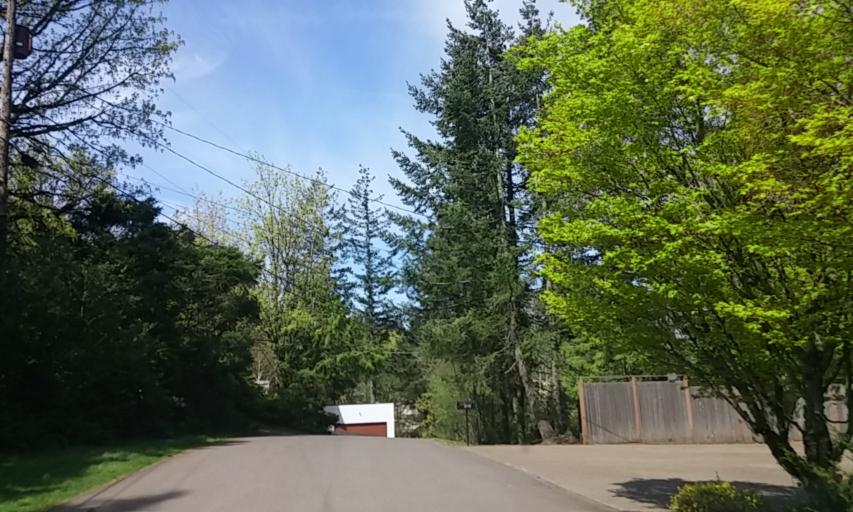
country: US
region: Oregon
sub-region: Washington County
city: West Haven-Sylvan
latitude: 45.5149
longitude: -122.7488
